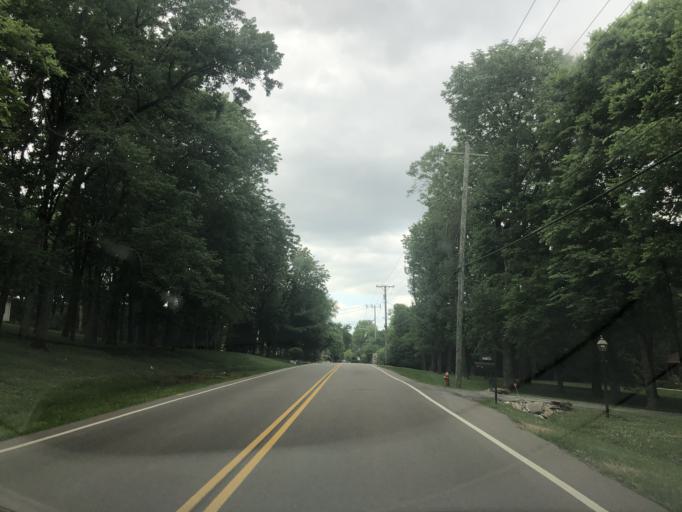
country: US
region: Tennessee
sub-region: Davidson County
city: Forest Hills
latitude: 36.0891
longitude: -86.8200
